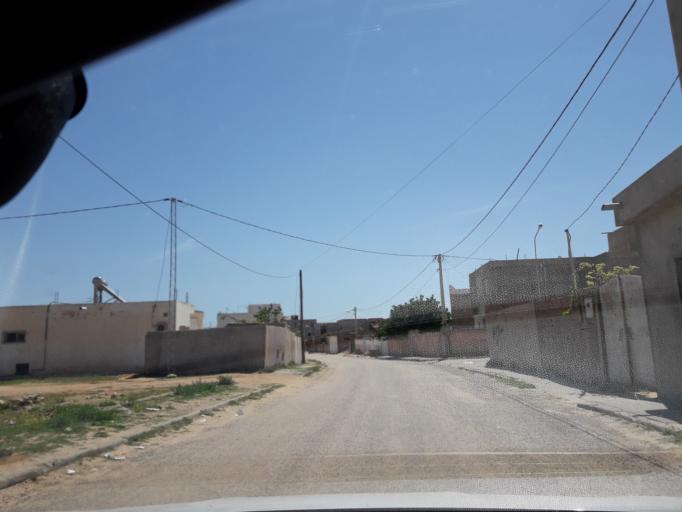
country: TN
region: Safaqis
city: Sfax
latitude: 34.7422
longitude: 10.5203
